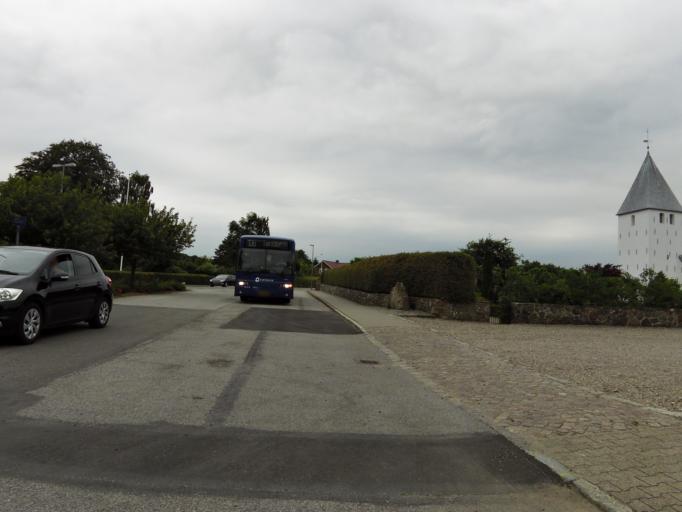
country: DK
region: South Denmark
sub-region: Tonder Kommune
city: Logumkloster
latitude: 55.0757
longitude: 8.9303
